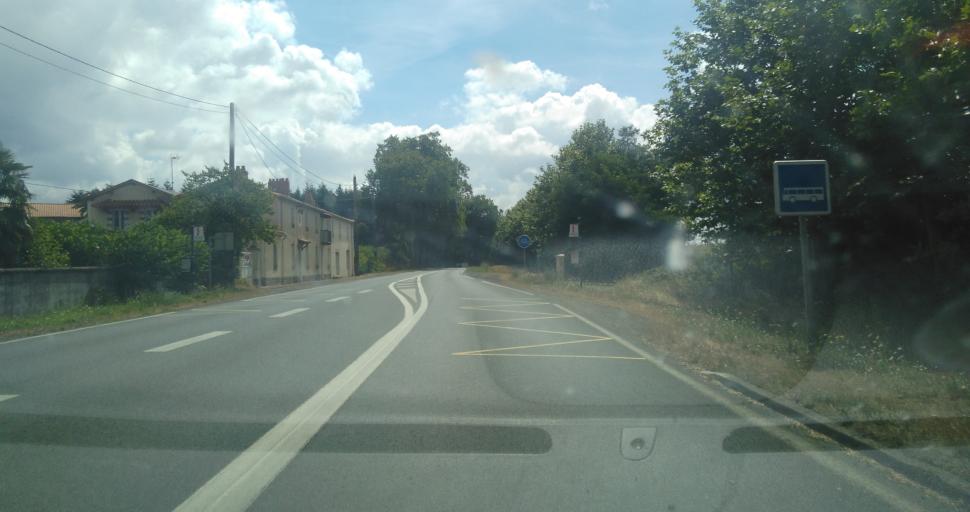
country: FR
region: Pays de la Loire
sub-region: Departement de la Vendee
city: Sainte-Hermine
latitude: 46.5638
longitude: -1.0769
